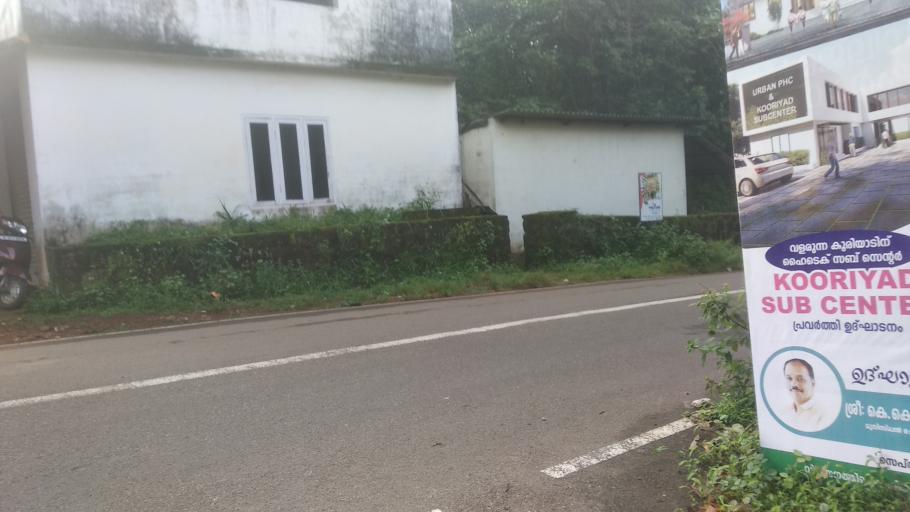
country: IN
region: Kerala
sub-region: Malappuram
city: Malappuram
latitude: 10.9920
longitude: 76.0472
